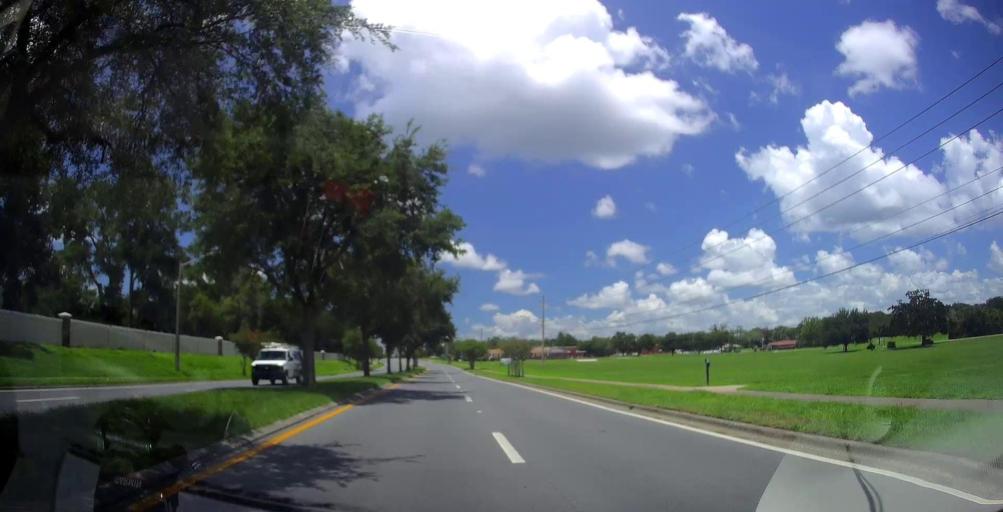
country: US
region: Florida
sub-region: Marion County
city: Ocala
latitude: 29.1788
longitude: -82.1030
